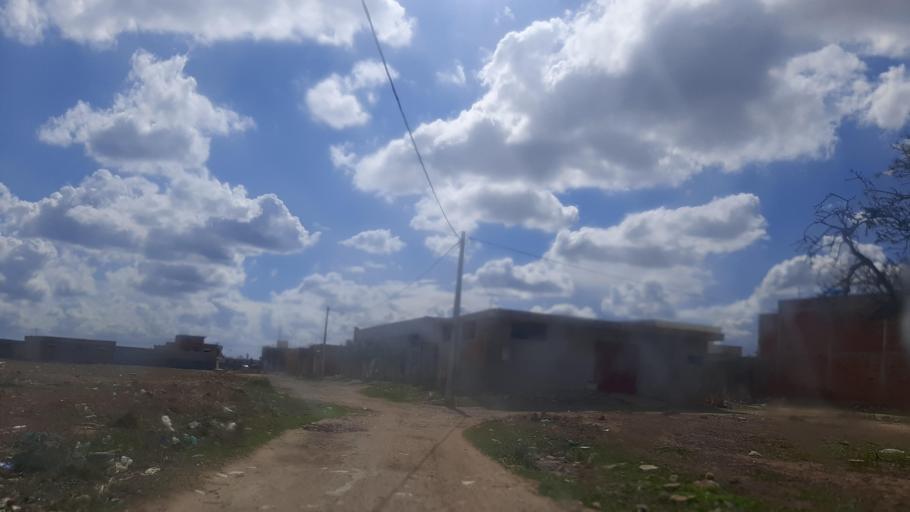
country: TN
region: Nabul
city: Korba
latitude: 36.5951
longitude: 10.8563
